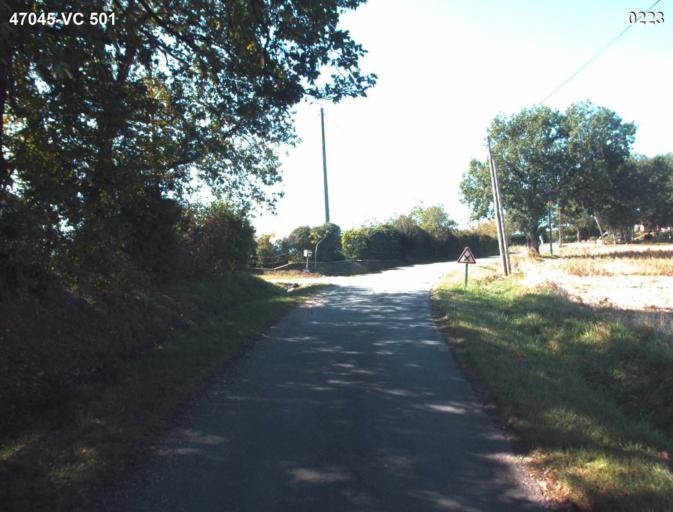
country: FR
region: Aquitaine
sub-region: Departement du Lot-et-Garonne
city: Nerac
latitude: 44.1537
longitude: 0.4035
